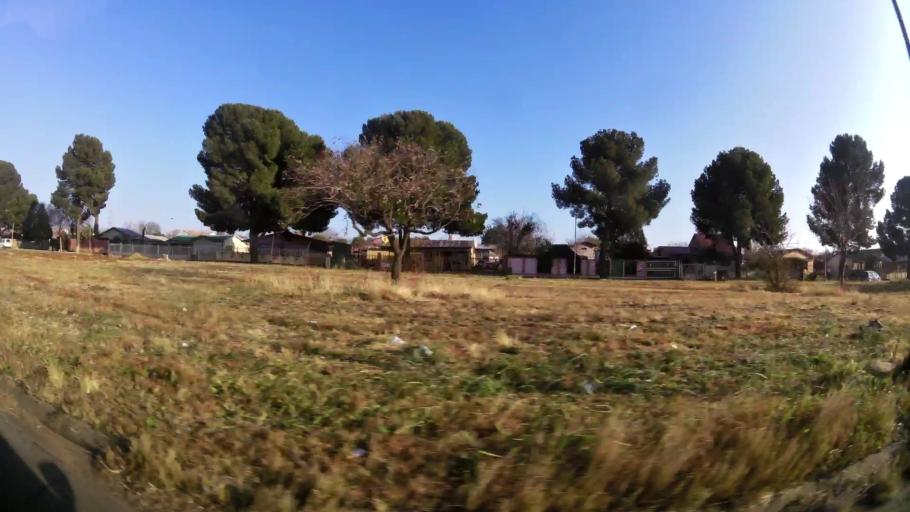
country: ZA
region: Orange Free State
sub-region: Mangaung Metropolitan Municipality
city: Bloemfontein
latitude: -29.1630
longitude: 26.2023
